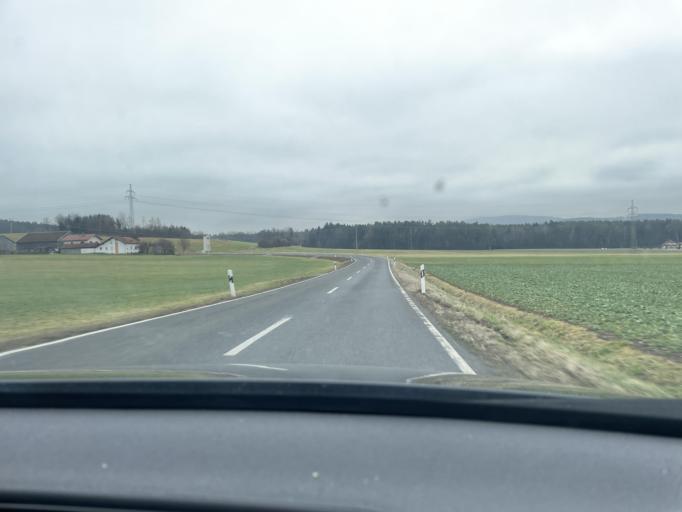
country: DE
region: Bavaria
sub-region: Upper Palatinate
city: Cham
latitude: 49.1900
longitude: 12.6933
